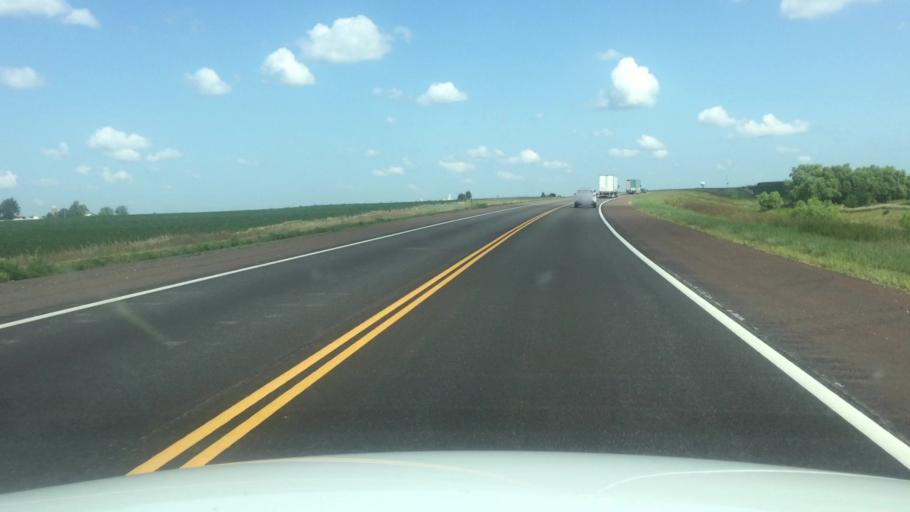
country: US
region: Kansas
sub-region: Nemaha County
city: Sabetha
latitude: 39.8735
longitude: -95.7799
